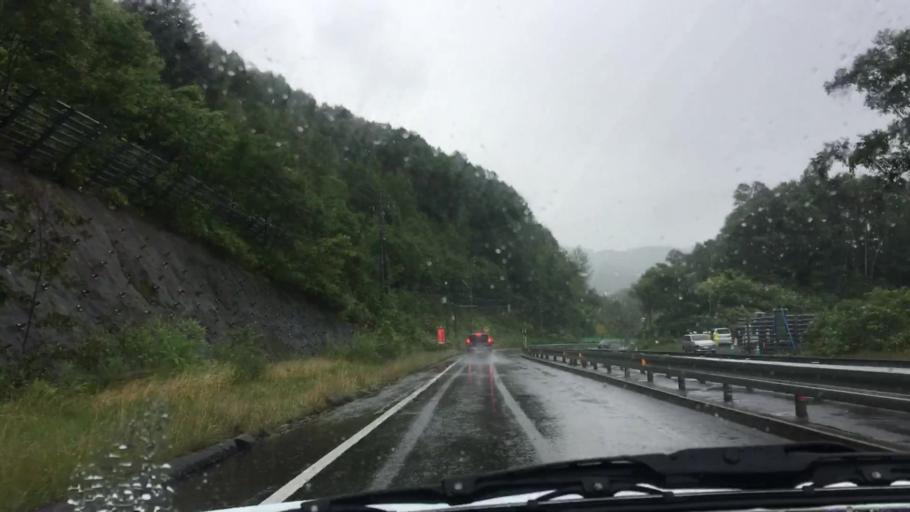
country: JP
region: Hokkaido
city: Otaru
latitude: 42.8509
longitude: 141.0695
